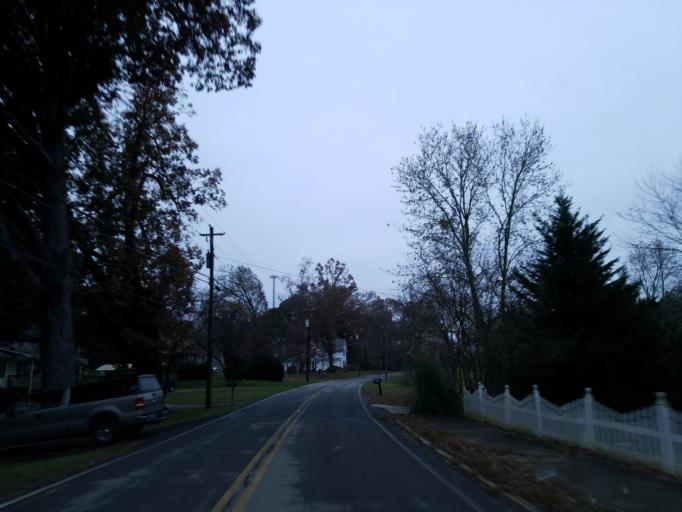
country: US
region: Georgia
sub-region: Cherokee County
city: Ball Ground
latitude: 34.3451
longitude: -84.3778
